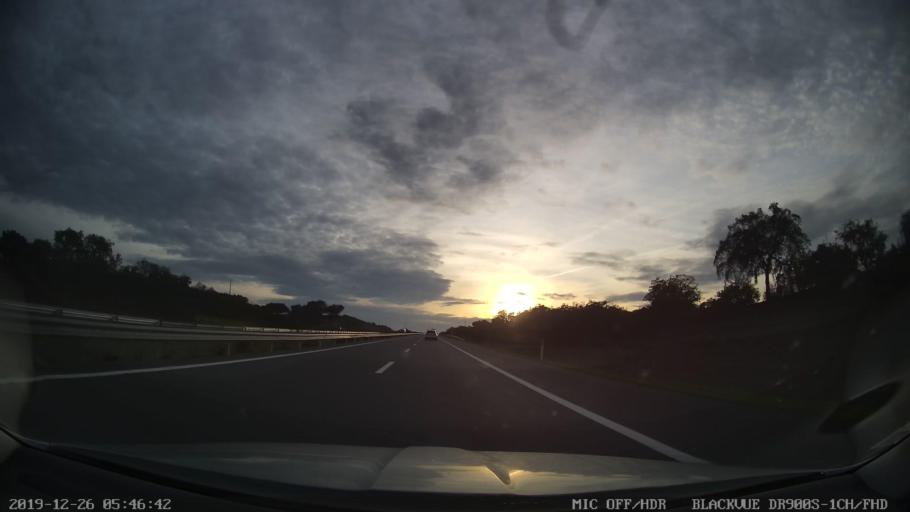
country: PT
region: Evora
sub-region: Estremoz
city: Estremoz
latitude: 38.7369
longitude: -7.7616
